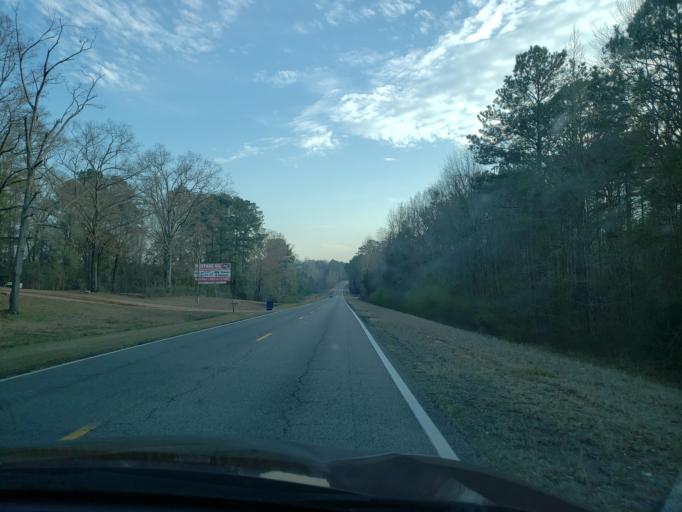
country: US
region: Alabama
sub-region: Hale County
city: Greensboro
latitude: 32.7417
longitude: -87.5855
